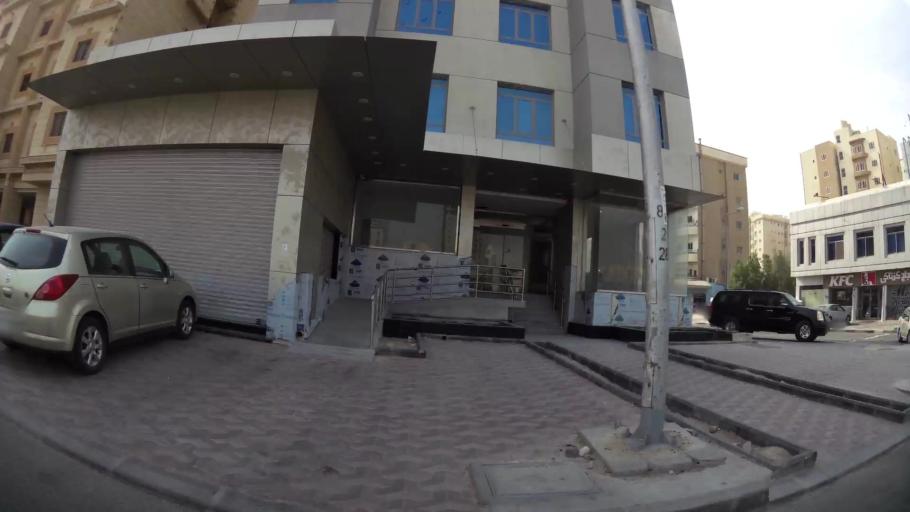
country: KW
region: Al Farwaniyah
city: Al Farwaniyah
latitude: 29.2761
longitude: 47.9598
